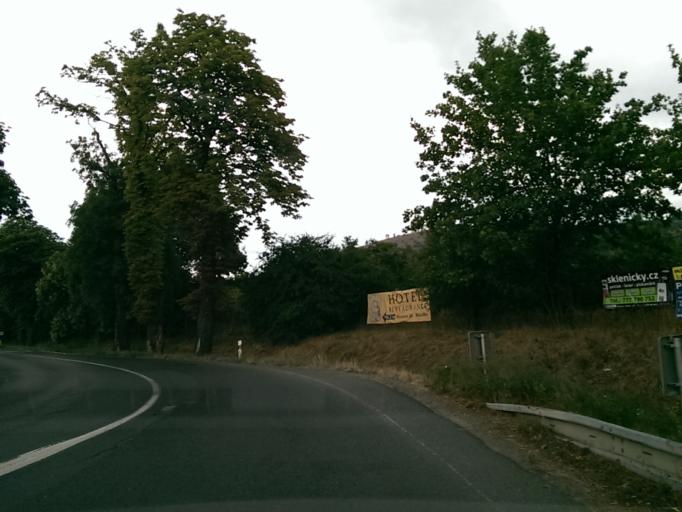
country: CZ
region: South Moravian
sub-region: Okres Breclav
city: Mikulov
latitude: 48.7992
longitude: 16.6501
